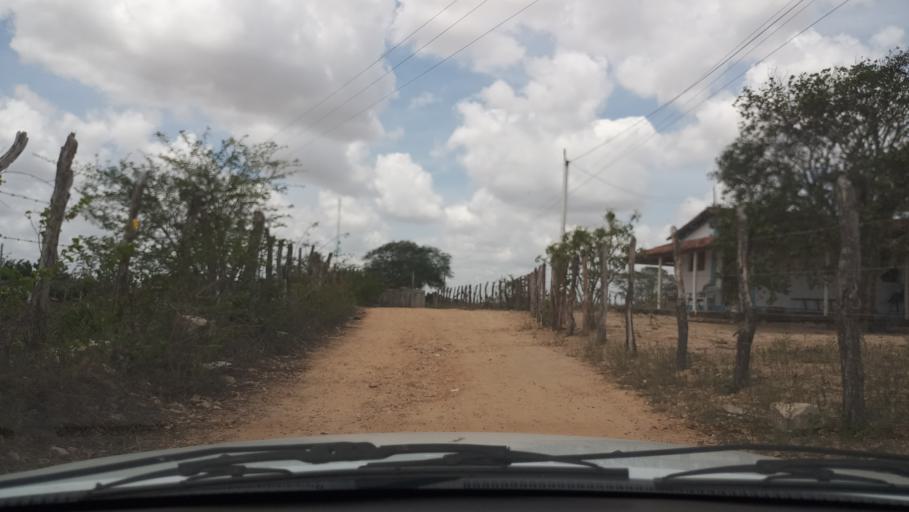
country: BR
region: Rio Grande do Norte
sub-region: Brejinho
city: Brejinho
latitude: -6.2707
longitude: -35.3455
